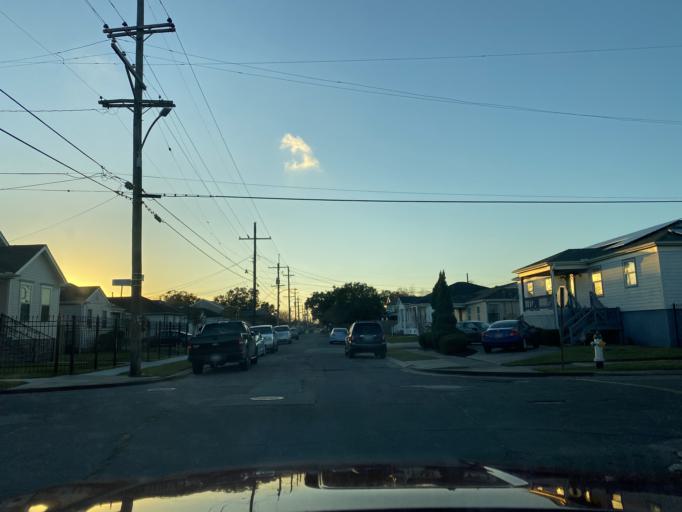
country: US
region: Louisiana
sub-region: Orleans Parish
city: New Orleans
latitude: 30.0193
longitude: -90.0538
